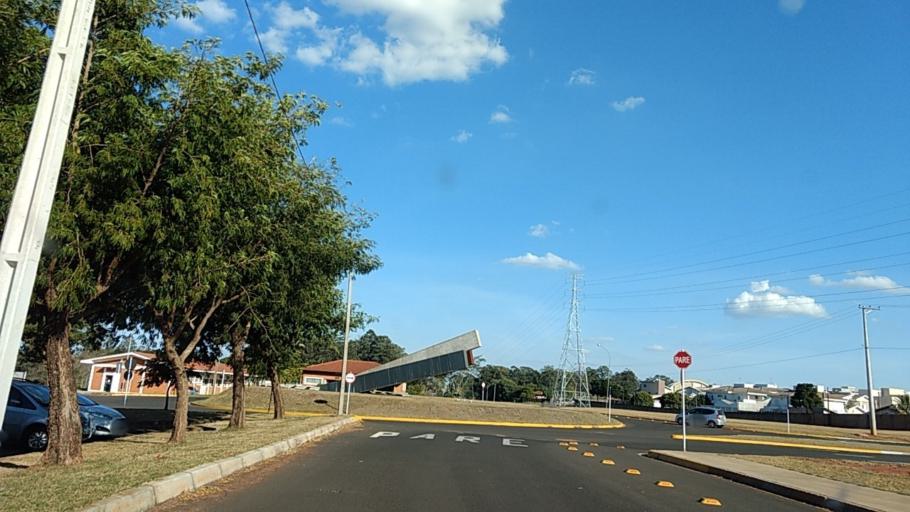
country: BR
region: Sao Paulo
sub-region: Botucatu
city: Botucatu
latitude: -22.8500
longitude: -48.4351
